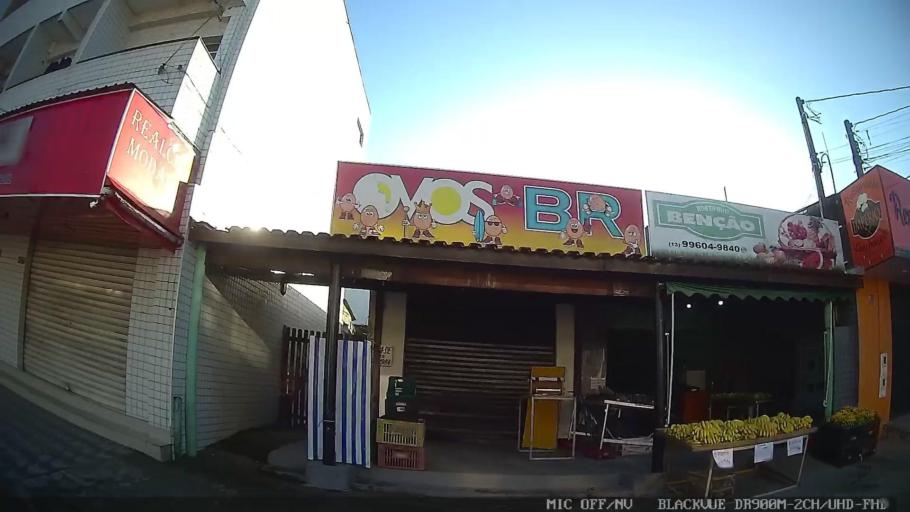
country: BR
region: Sao Paulo
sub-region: Itanhaem
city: Itanhaem
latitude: -24.2355
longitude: -46.9010
